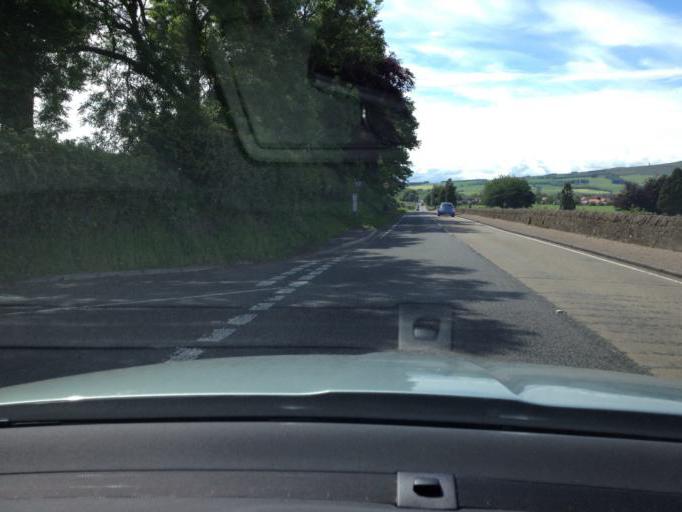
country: GB
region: Scotland
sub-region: Fife
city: Ladybank
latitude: 56.2596
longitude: -3.1067
